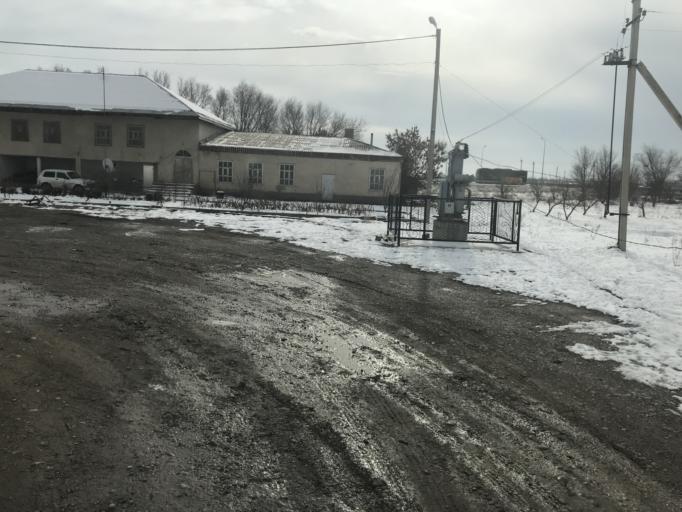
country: KZ
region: Ongtustik Qazaqstan
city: Aksu
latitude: 42.4752
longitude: 69.8180
